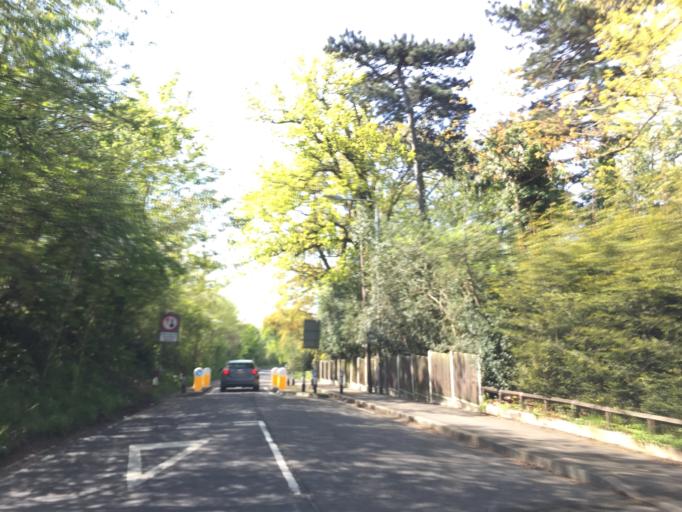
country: GB
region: England
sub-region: Greater London
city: Collier Row
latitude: 51.6127
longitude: 0.1808
